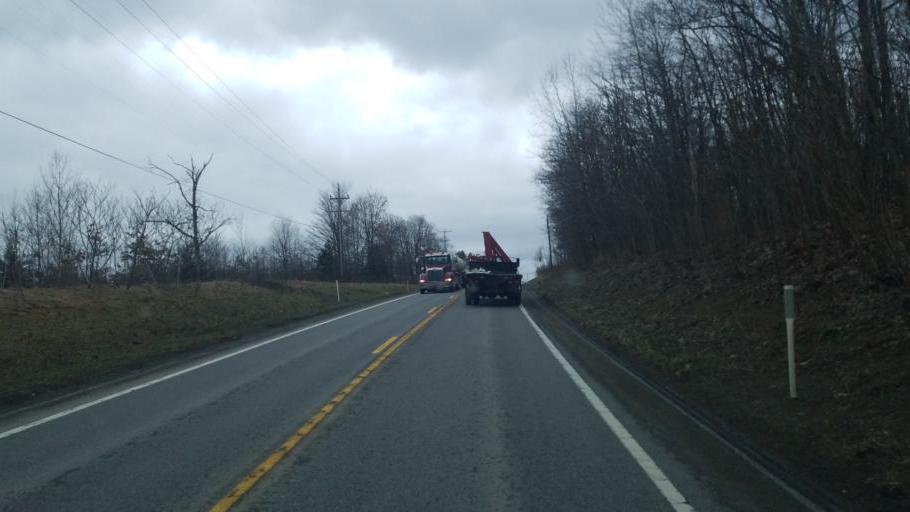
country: US
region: Pennsylvania
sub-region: Clarion County
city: Marianne
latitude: 41.3635
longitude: -79.3172
